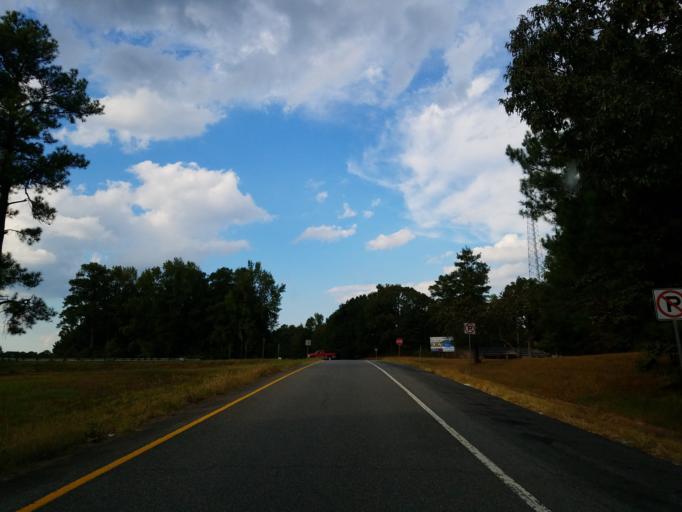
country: US
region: Georgia
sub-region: Monroe County
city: Forsyth
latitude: 33.1114
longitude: -84.0019
